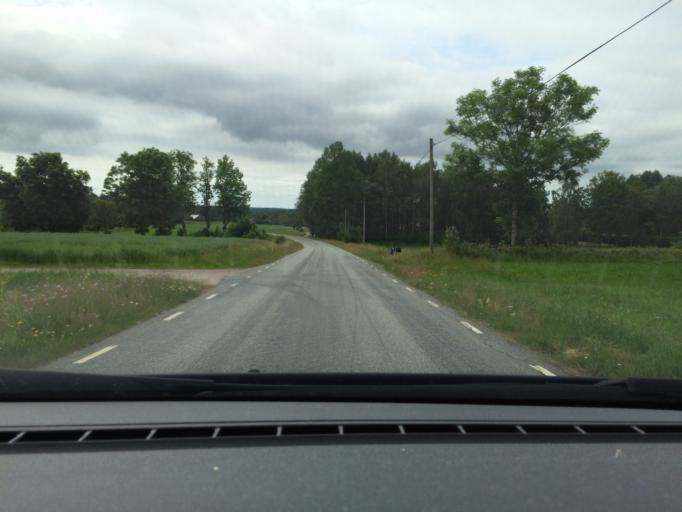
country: SE
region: Joenkoeping
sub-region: Varnamo Kommun
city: Forsheda
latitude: 57.1069
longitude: 13.8052
